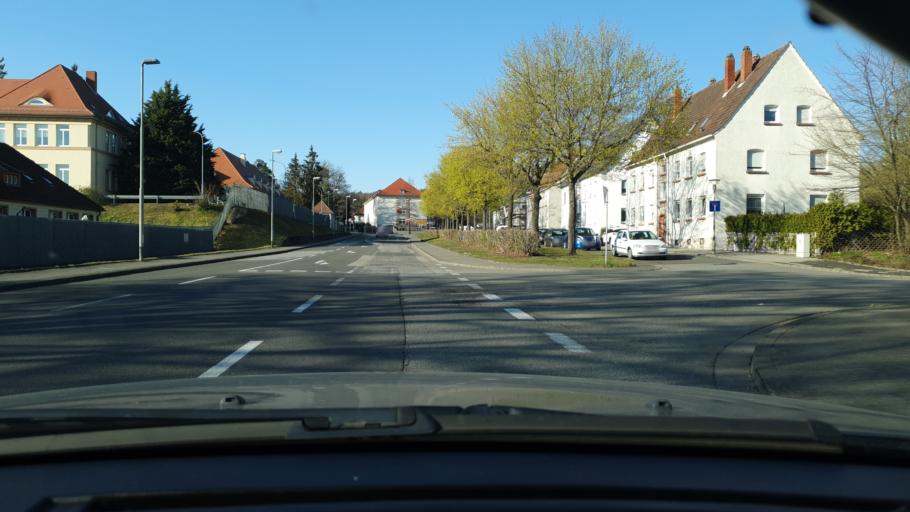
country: DE
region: Rheinland-Pfalz
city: Kaiserslautern
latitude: 49.4418
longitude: 7.8104
